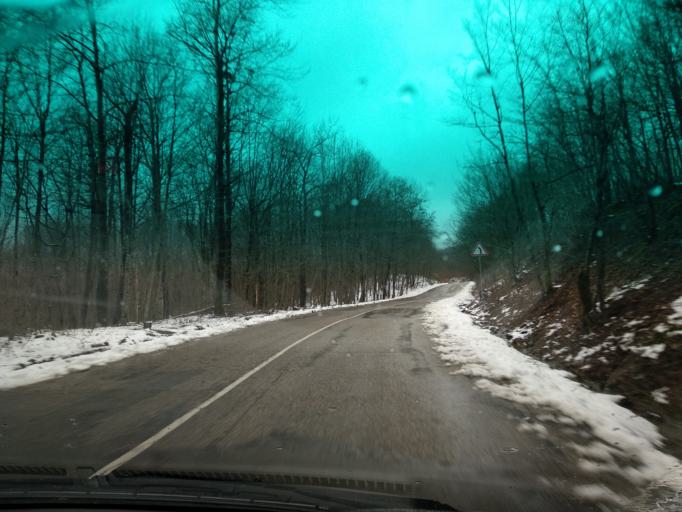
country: RU
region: Krasnodarskiy
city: Khadyzhensk
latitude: 44.2086
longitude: 39.4076
